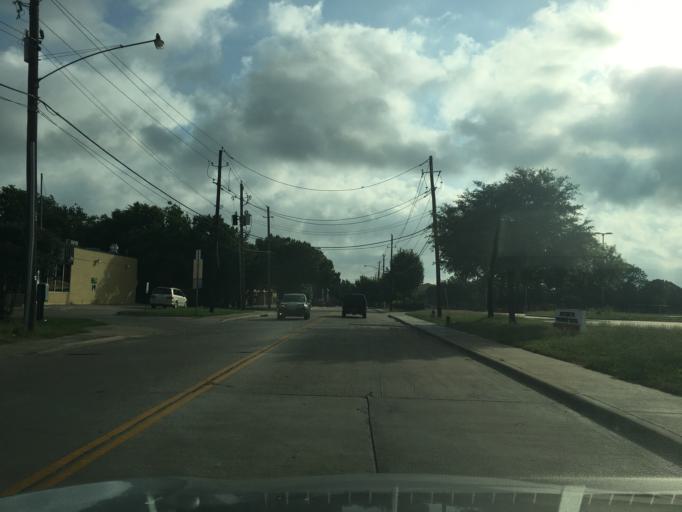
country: US
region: Texas
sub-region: Dallas County
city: University Park
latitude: 32.8730
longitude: -96.7620
